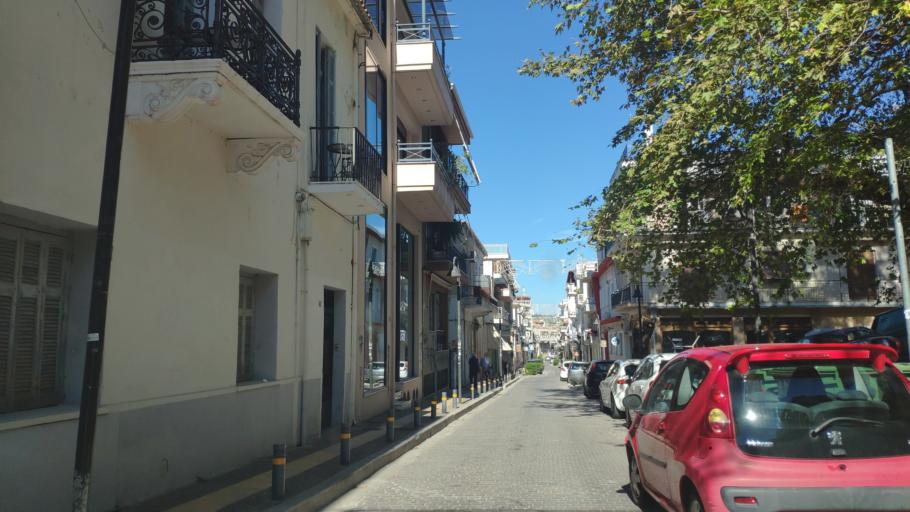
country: GR
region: Central Greece
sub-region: Nomos Voiotias
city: Livadeia
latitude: 38.4337
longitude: 22.8755
